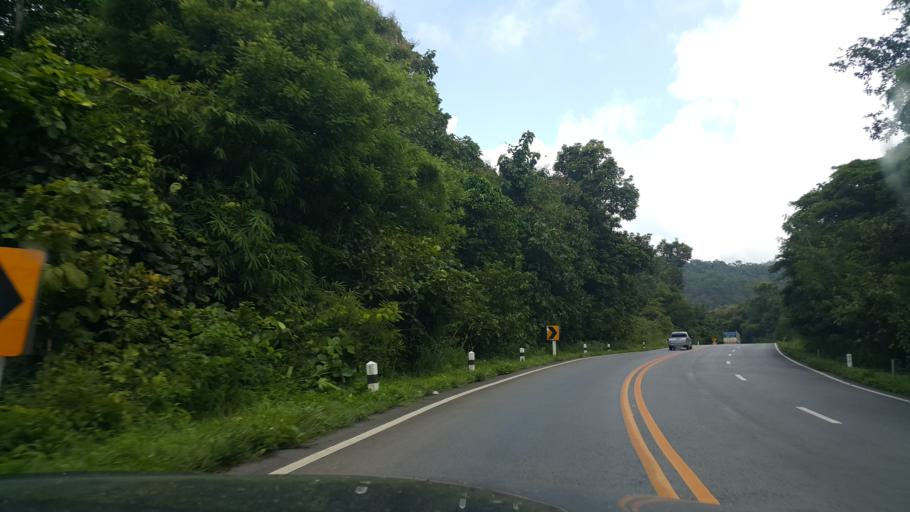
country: TH
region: Chiang Mai
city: Mae On
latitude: 18.9306
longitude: 99.2370
